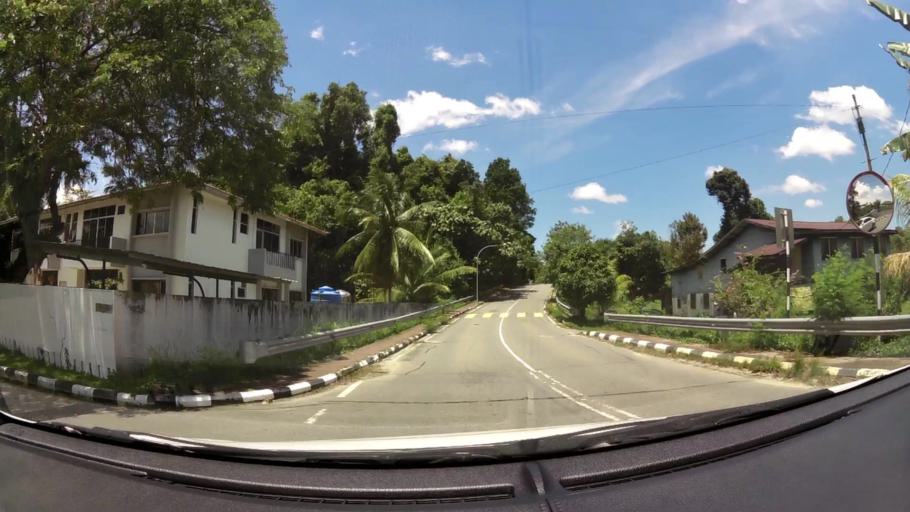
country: BN
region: Brunei and Muara
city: Bandar Seri Begawan
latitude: 4.9416
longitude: 114.9606
